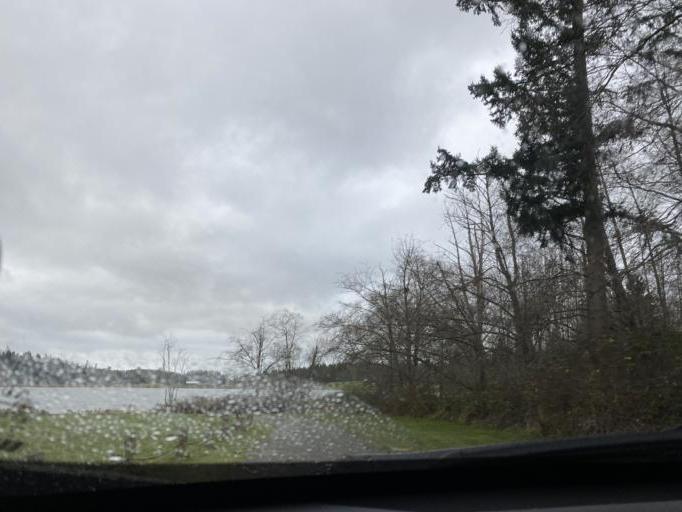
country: US
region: Washington
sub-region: Island County
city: Langley
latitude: 48.0247
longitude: -122.4613
